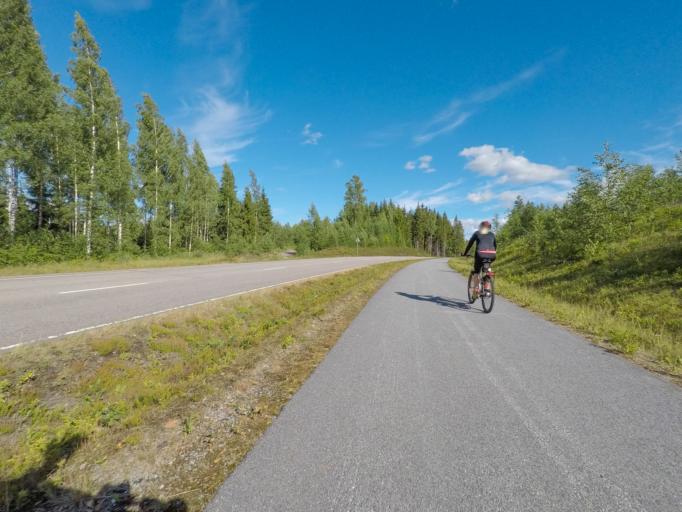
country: FI
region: South Karelia
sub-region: Lappeenranta
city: Joutseno
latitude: 61.1531
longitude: 28.6110
